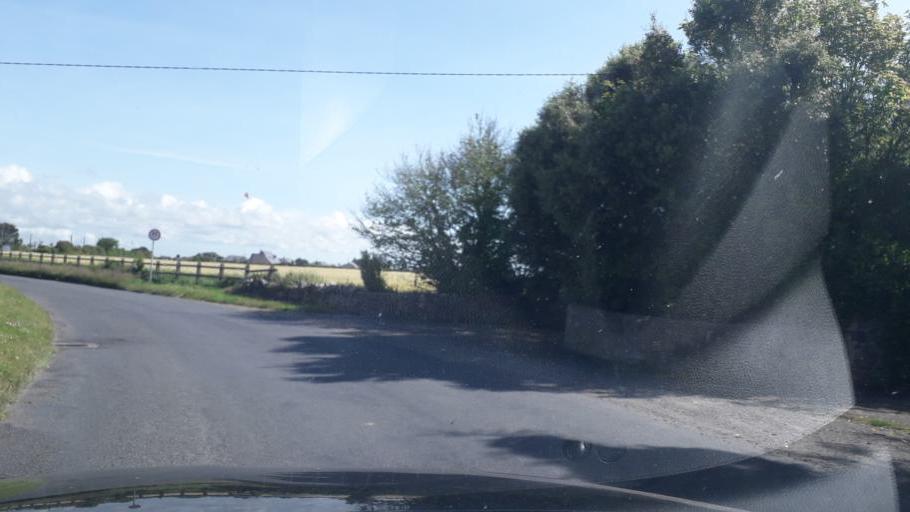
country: IE
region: Leinster
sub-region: Loch Garman
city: Loch Garman
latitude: 52.1811
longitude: -6.5821
